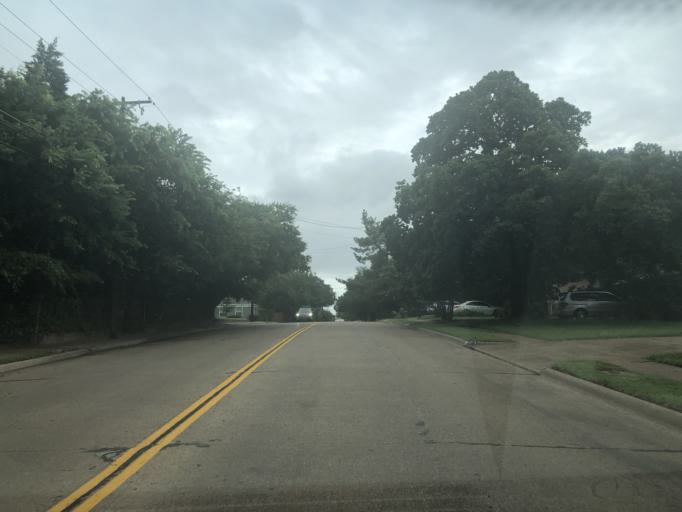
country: US
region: Texas
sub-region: Dallas County
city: Irving
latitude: 32.7992
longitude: -96.9469
